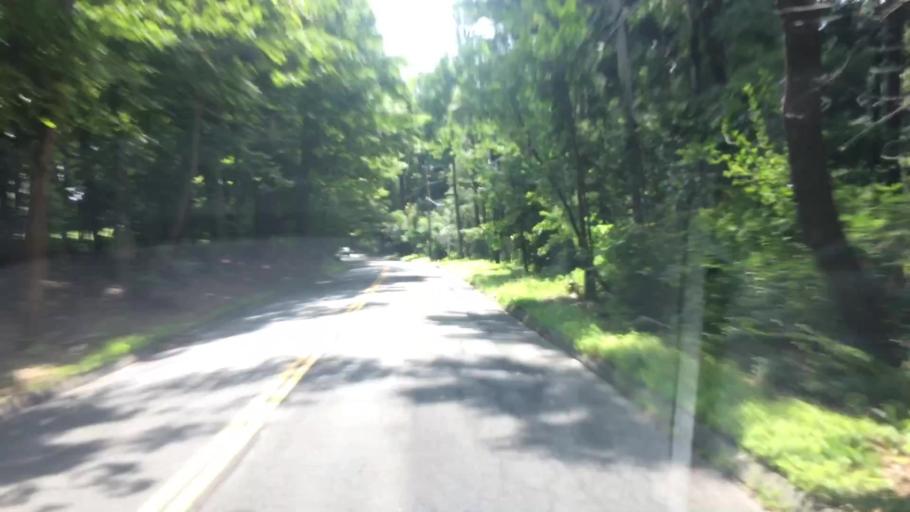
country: US
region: Connecticut
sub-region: Fairfield County
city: Danbury
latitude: 41.4062
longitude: -73.4781
